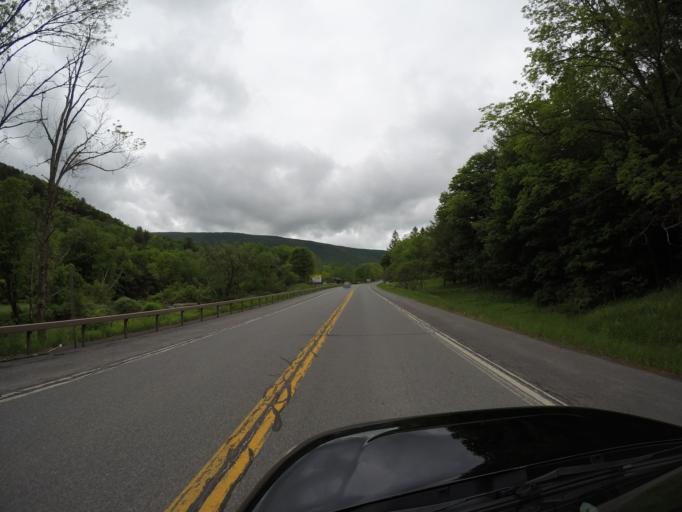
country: US
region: New York
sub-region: Delaware County
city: Stamford
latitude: 42.1524
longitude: -74.5996
